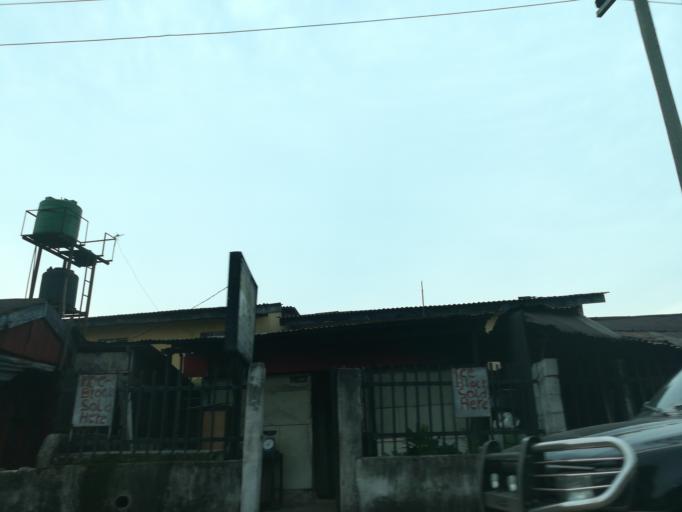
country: NG
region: Rivers
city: Port Harcourt
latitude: 4.8201
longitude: 7.0244
